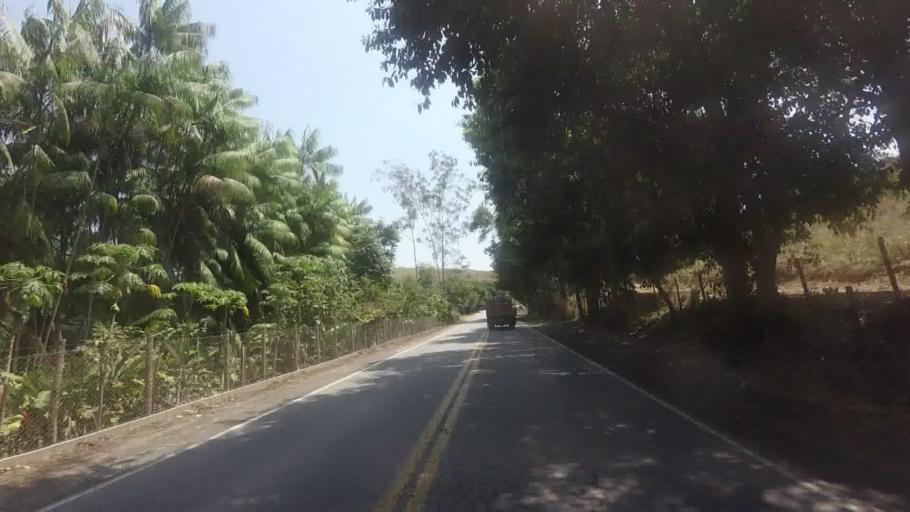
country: BR
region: Espirito Santo
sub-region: Rio Novo Do Sul
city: Rio Novo do Sul
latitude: -20.8793
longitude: -41.0117
